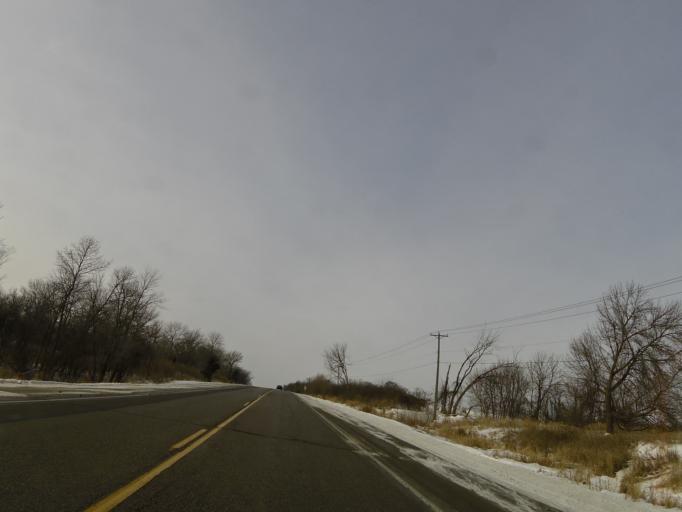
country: US
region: Minnesota
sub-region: Carver County
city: Victoria
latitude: 44.8913
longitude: -93.6937
